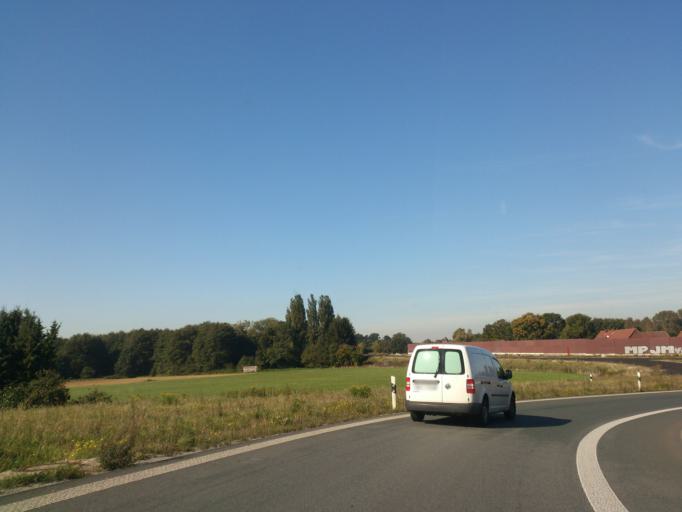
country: DE
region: North Rhine-Westphalia
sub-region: Regierungsbezirk Detmold
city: Bielefeld
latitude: 51.9722
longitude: 8.4783
